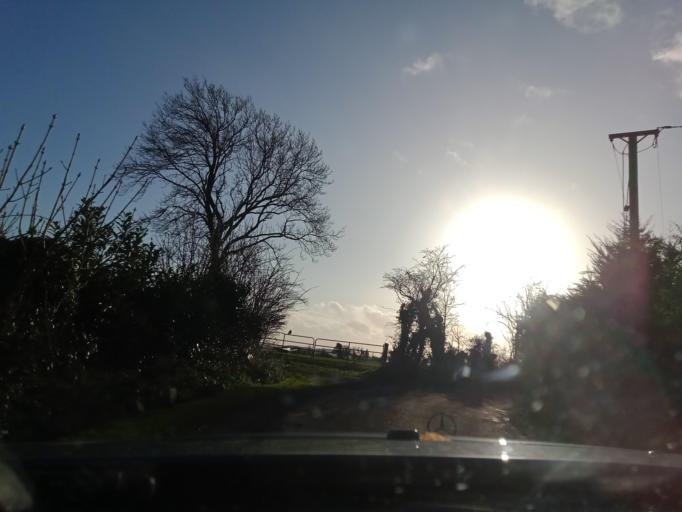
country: IE
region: Leinster
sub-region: Kilkenny
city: Callan
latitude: 52.4920
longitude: -7.3931
